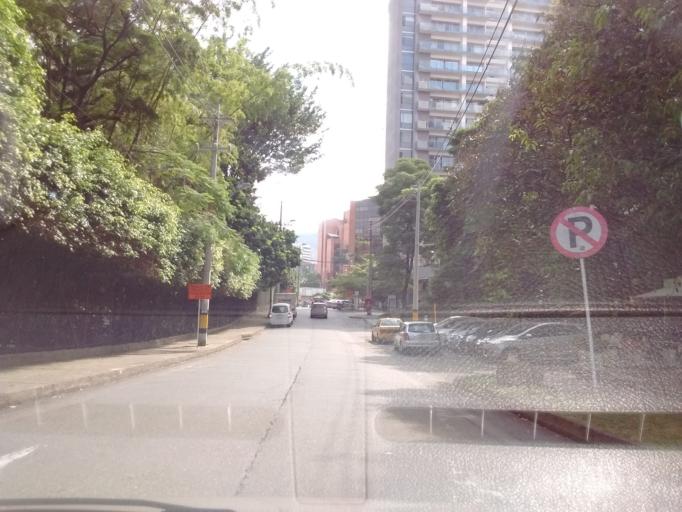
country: CO
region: Antioquia
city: Itagui
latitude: 6.2011
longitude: -75.5744
